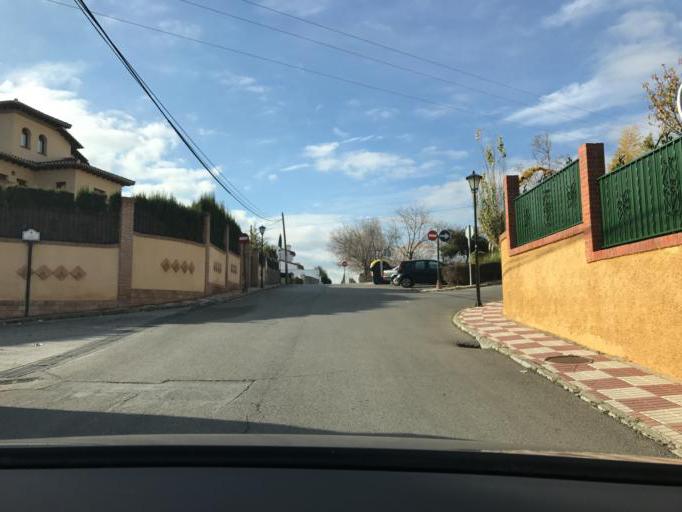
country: ES
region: Andalusia
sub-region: Provincia de Granada
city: Otura
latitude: 37.0874
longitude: -3.6279
